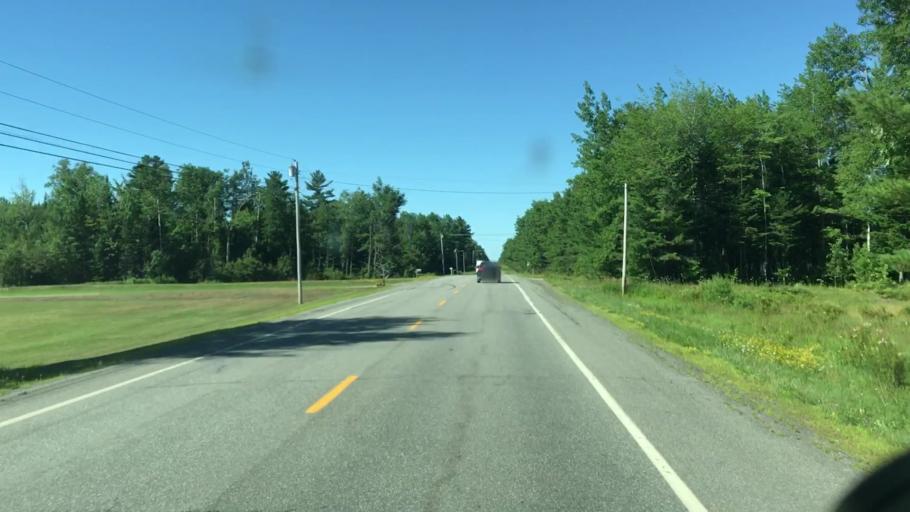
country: US
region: Maine
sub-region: Penobscot County
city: Enfield
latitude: 45.3216
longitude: -68.5980
